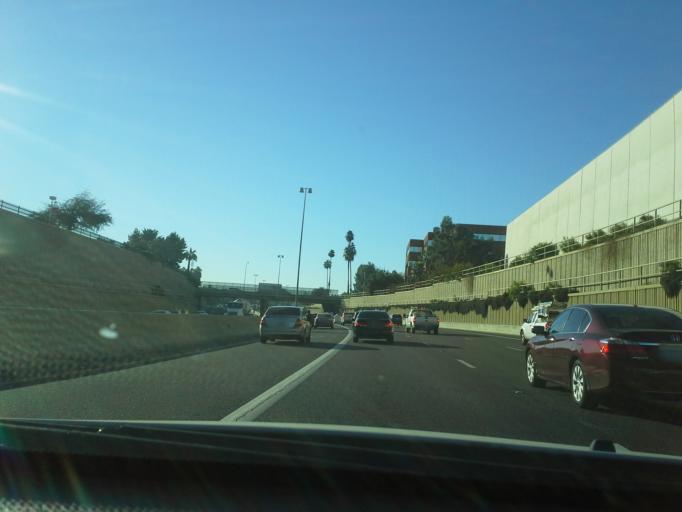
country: US
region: Arizona
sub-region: Maricopa County
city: Phoenix
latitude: 33.5077
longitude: -112.0444
